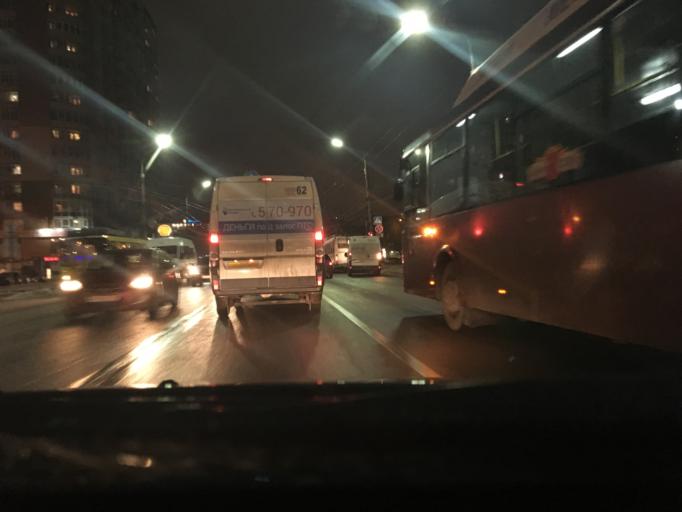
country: RU
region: Tula
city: Mendeleyevskiy
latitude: 54.1540
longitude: 37.5844
